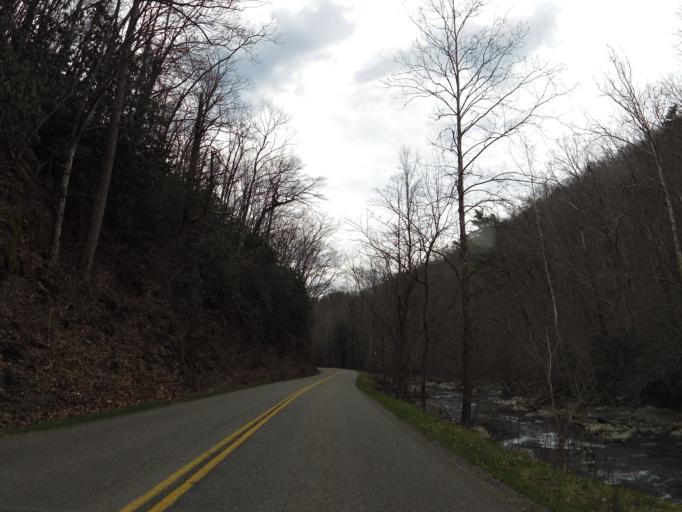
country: US
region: Tennessee
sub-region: Sevier County
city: Gatlinburg
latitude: 35.6679
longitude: -83.6367
